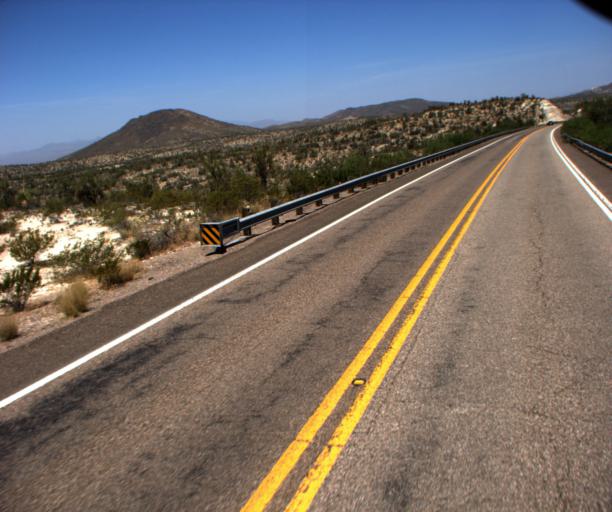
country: US
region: Arizona
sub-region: Gila County
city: Peridot
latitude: 33.2587
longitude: -110.2944
